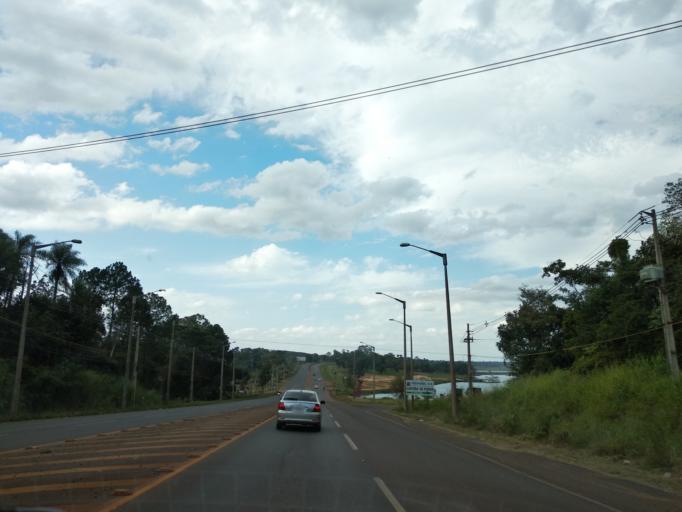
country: PY
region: Itapua
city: San Juan del Parana
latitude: -27.2921
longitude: -55.9209
